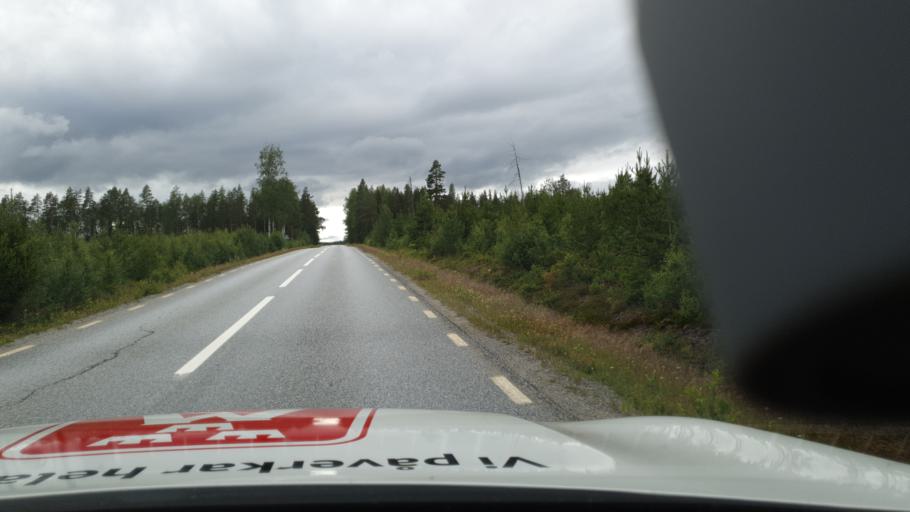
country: SE
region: Vaesterbotten
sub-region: Skelleftea Kommun
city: Burtraesk
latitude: 64.4020
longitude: 20.3770
